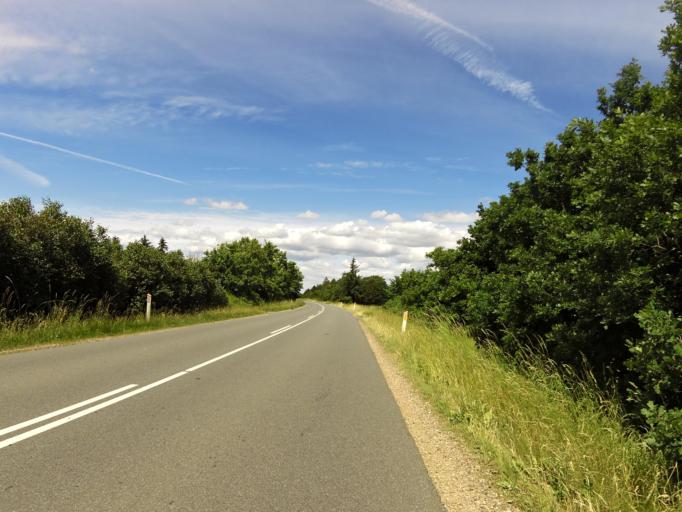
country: DK
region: South Denmark
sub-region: Esbjerg Kommune
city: Ribe
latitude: 55.3055
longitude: 8.7676
